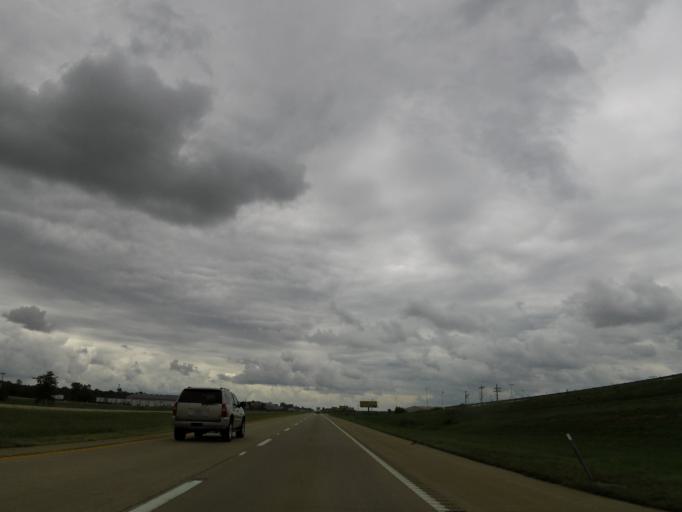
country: US
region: Missouri
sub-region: Mississippi County
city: Charleston
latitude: 36.9214
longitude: -89.3179
